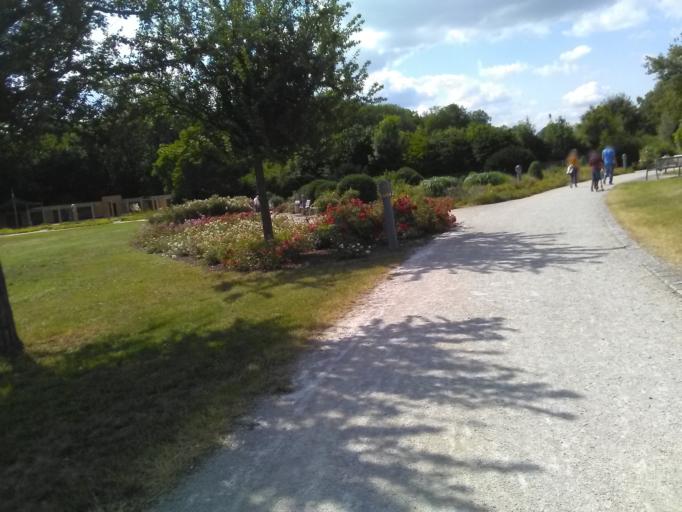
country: DE
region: Bavaria
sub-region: Upper Franconia
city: Bad Staffelstein
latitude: 50.1108
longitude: 10.9862
